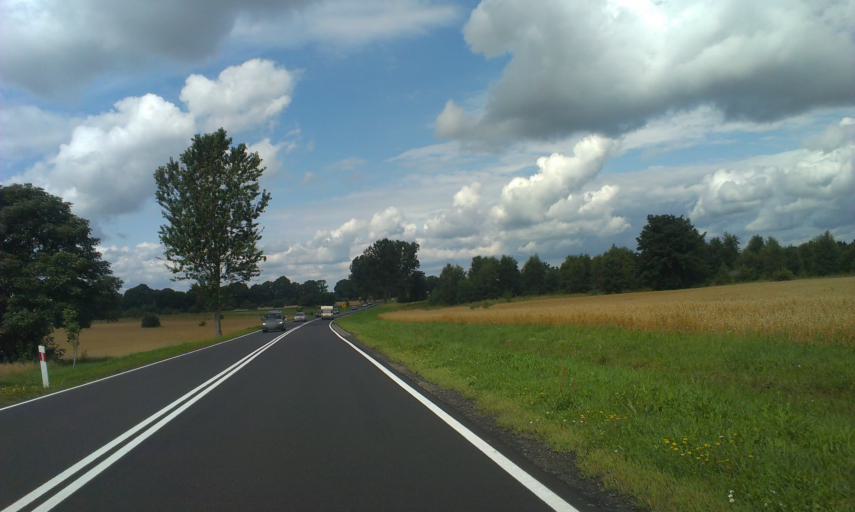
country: PL
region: West Pomeranian Voivodeship
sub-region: Powiat koszalinski
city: Bobolice
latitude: 54.0226
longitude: 16.4749
